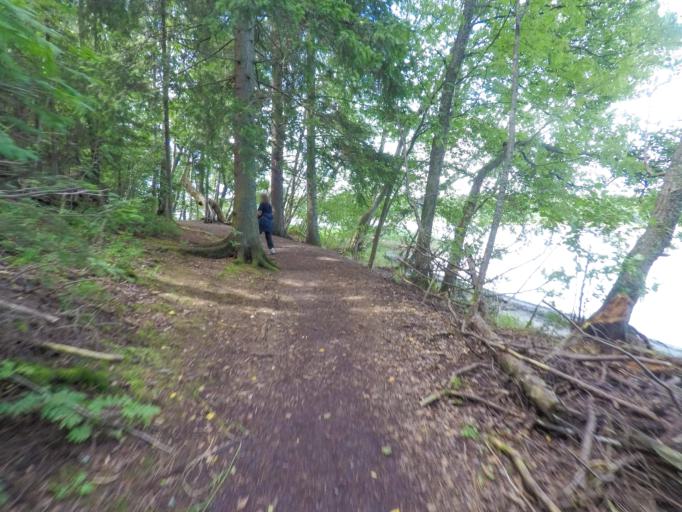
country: FI
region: Uusimaa
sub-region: Helsinki
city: Vantaa
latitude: 60.1675
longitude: 25.0722
